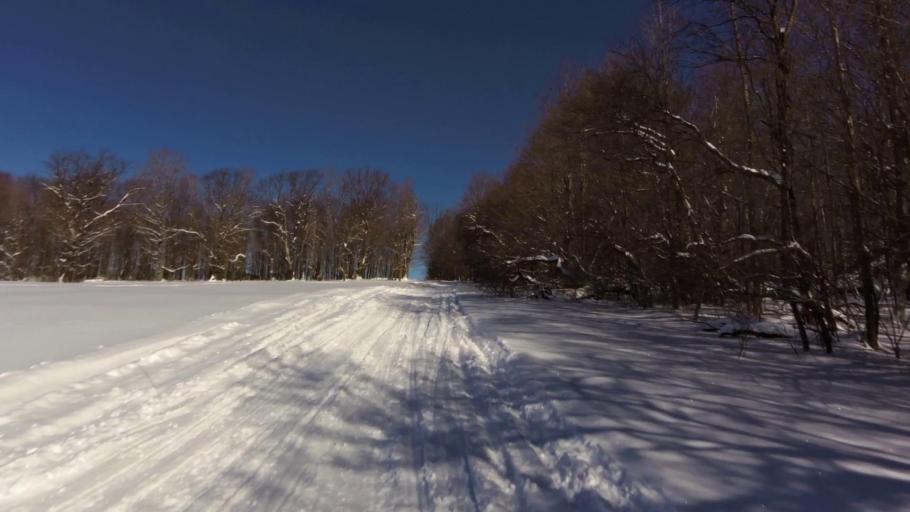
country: US
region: New York
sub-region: Chautauqua County
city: Silver Creek
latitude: 42.3801
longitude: -79.1497
